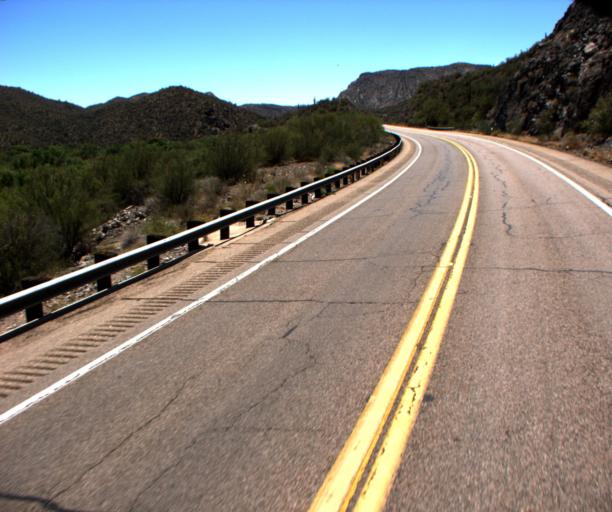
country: US
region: Arizona
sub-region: Pinal County
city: Kearny
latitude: 33.0239
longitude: -110.7366
